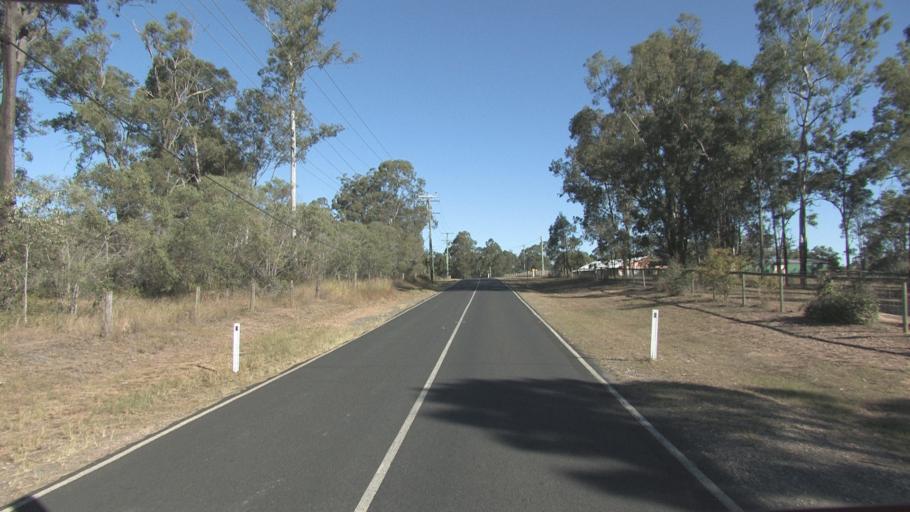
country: AU
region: Queensland
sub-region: Logan
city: Park Ridge South
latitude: -27.7372
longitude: 153.0176
